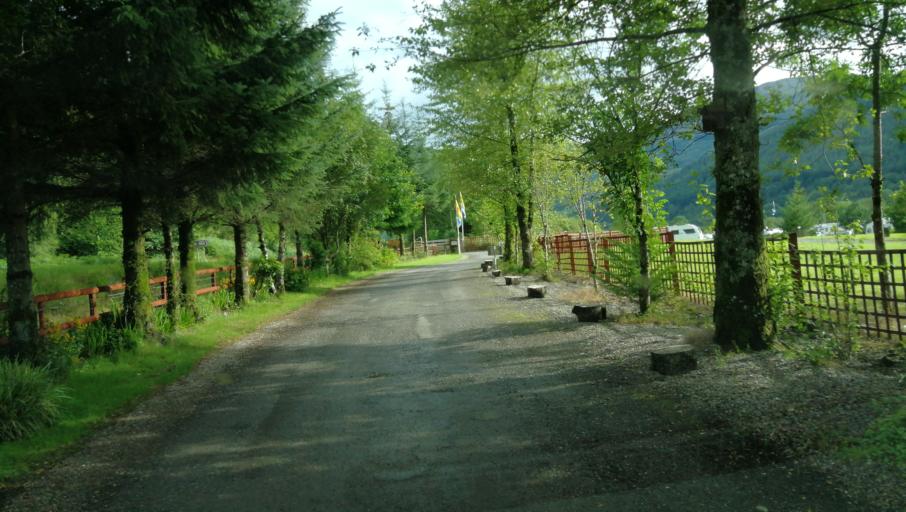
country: GB
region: Scotland
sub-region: Stirling
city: Callander
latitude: 56.3183
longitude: -4.3296
